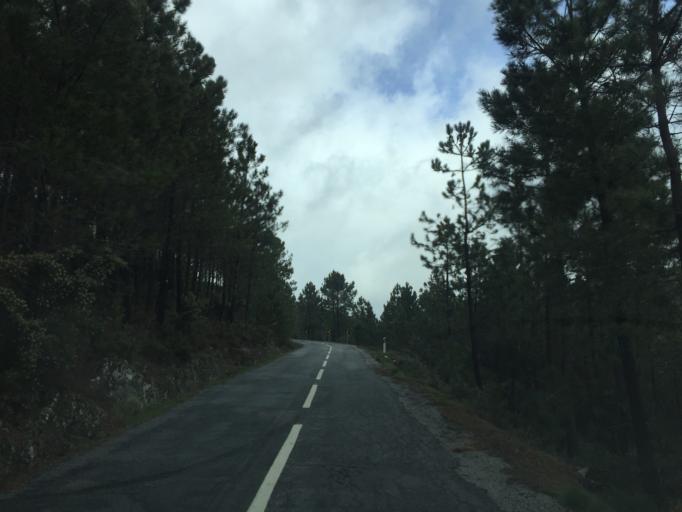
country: PT
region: Guarda
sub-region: Seia
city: Seia
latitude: 40.3298
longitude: -7.7150
